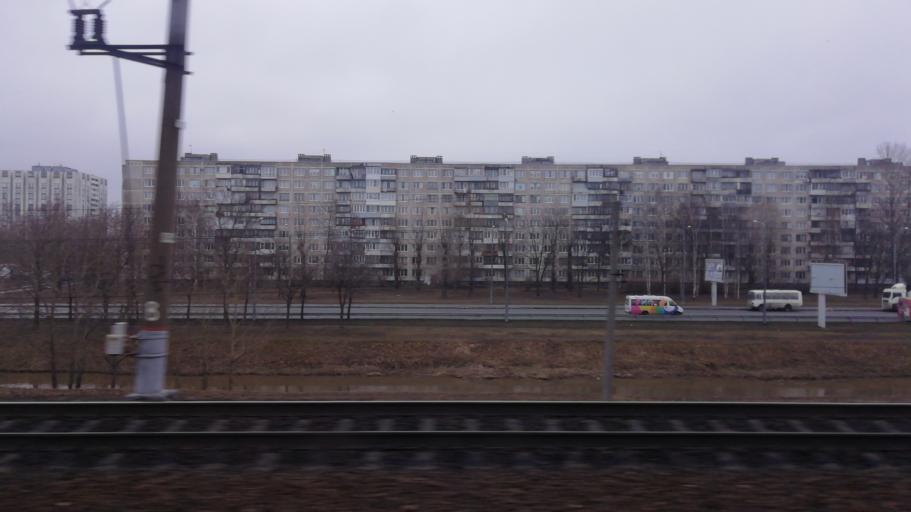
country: RU
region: St.-Petersburg
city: Kupchino
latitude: 59.8709
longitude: 30.3560
